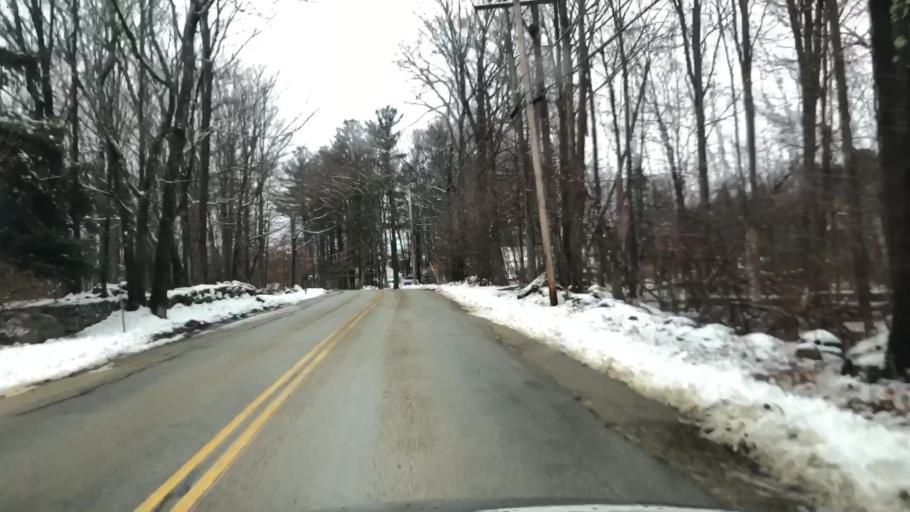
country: US
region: New Hampshire
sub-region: Hillsborough County
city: Mont Vernon
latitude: 42.9212
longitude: -71.6007
